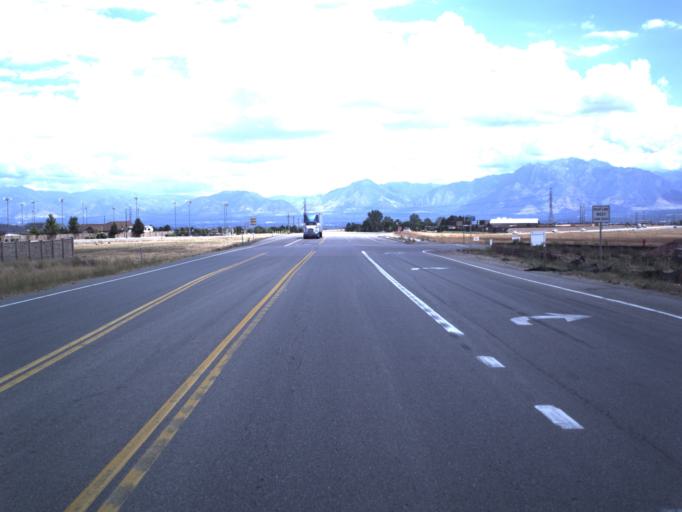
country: US
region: Utah
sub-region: Salt Lake County
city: Oquirrh
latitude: 40.5862
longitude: -112.0400
